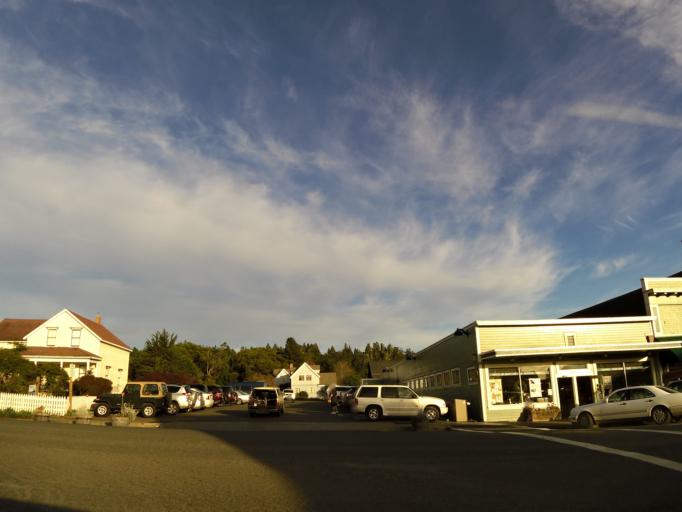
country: US
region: California
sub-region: Mendocino County
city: Fort Bragg
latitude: 39.3075
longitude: -123.7991
